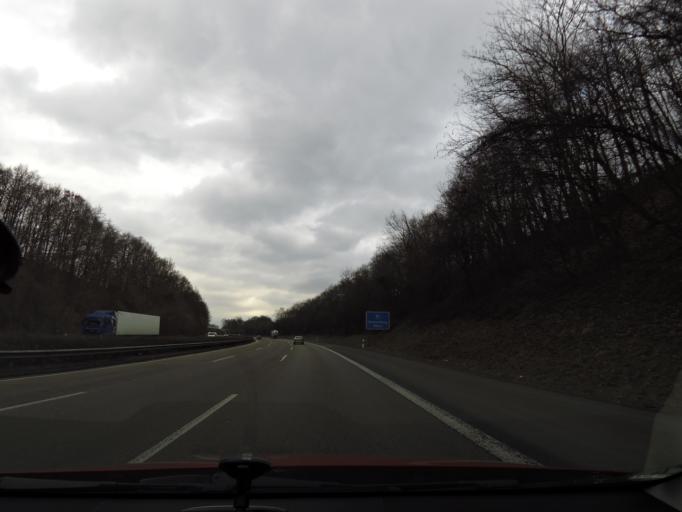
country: DE
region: Rheinland-Pfalz
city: Weitersburg
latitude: 50.4087
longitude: 7.6077
